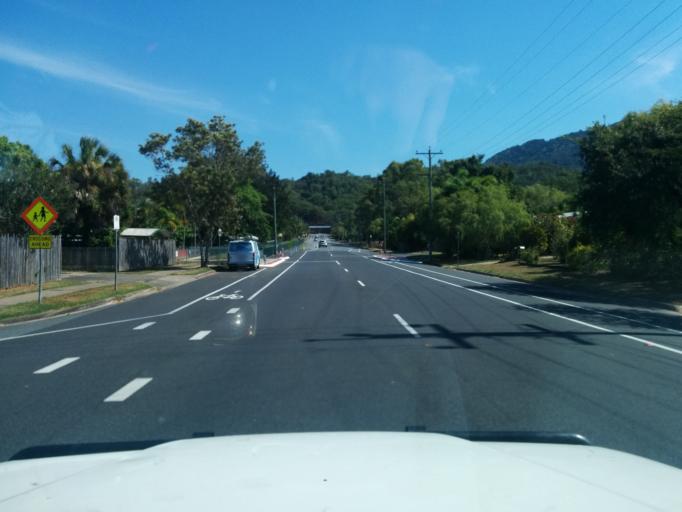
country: AU
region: Queensland
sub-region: Cairns
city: Redlynch
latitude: -16.9097
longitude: 145.7282
